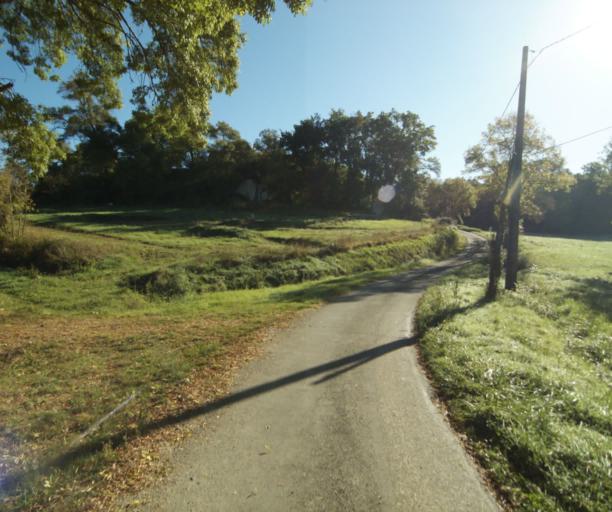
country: FR
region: Midi-Pyrenees
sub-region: Departement du Gers
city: Gondrin
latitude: 43.8387
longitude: 0.2500
